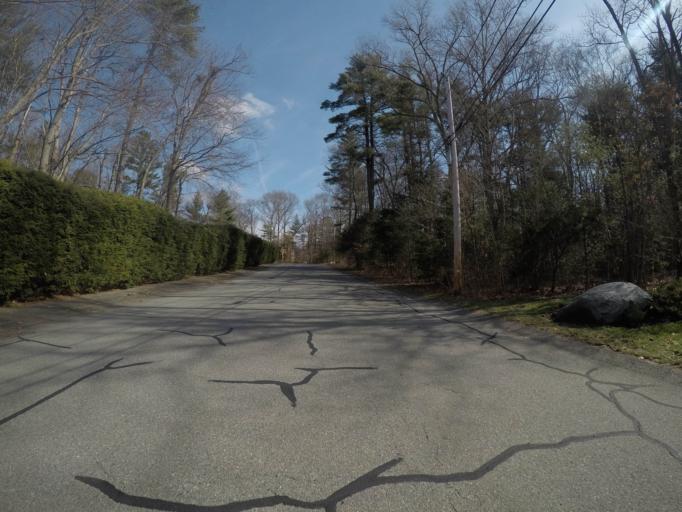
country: US
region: Massachusetts
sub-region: Bristol County
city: Easton
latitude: 42.0203
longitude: -71.1474
